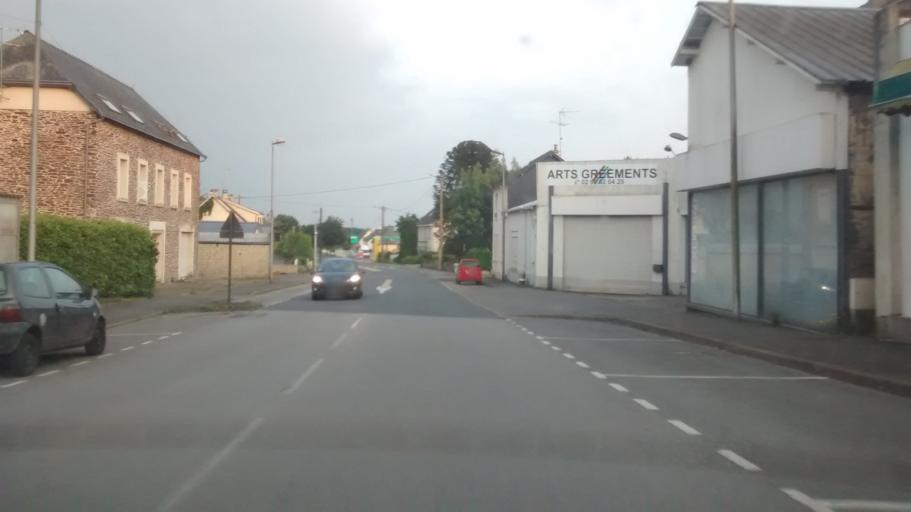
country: FR
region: Brittany
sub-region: Departement du Morbihan
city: Guer
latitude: 47.9397
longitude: -2.1332
